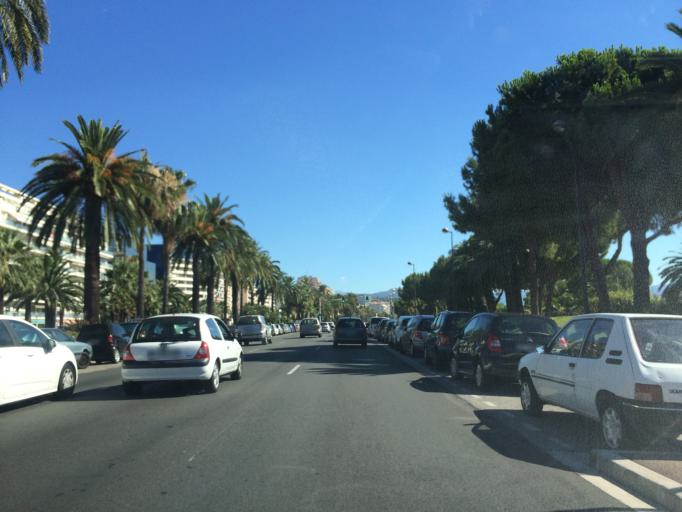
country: FR
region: Provence-Alpes-Cote d'Azur
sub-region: Departement des Alpes-Maritimes
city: Nice
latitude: 43.6765
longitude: 7.2285
